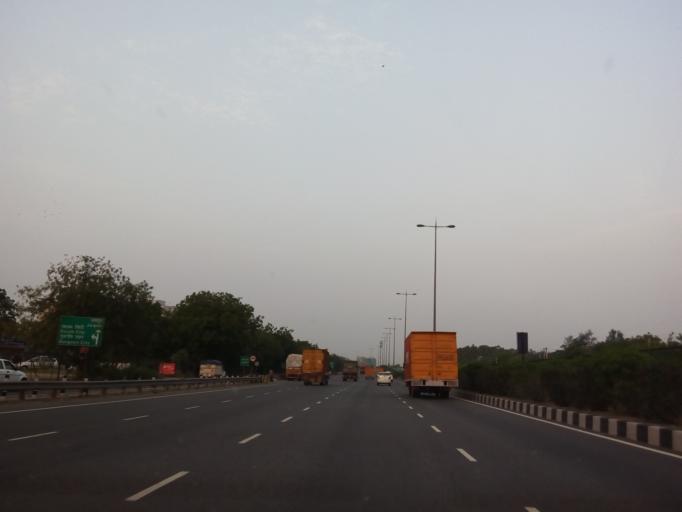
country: IN
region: Haryana
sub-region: Gurgaon
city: Gurgaon
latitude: 28.4718
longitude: 77.0614
